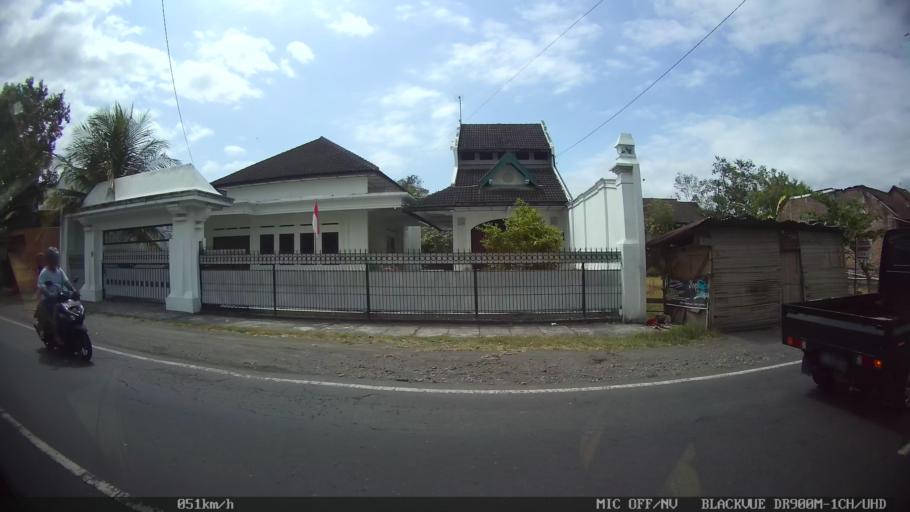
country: ID
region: Central Java
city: Candi Prambanan
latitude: -7.8217
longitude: 110.4802
